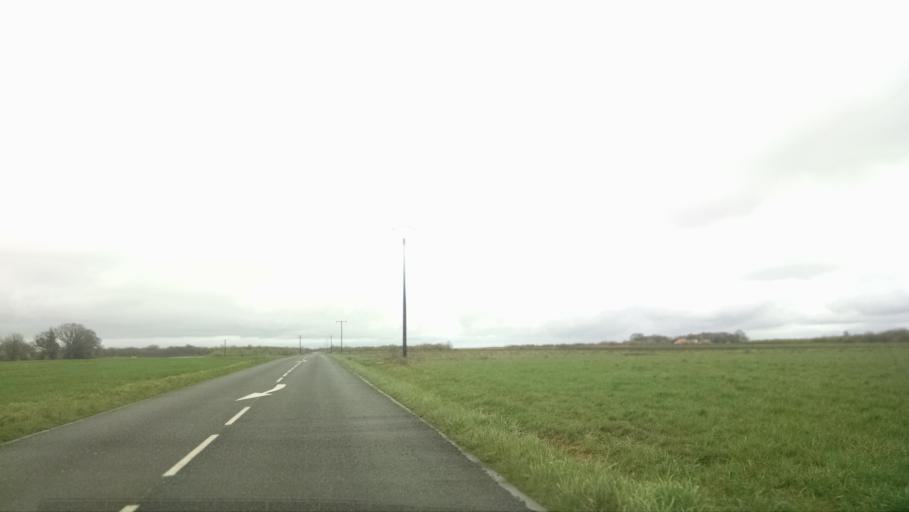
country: FR
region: Pays de la Loire
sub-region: Departement de la Loire-Atlantique
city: Maisdon-sur-Sevre
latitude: 47.1058
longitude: -1.3778
